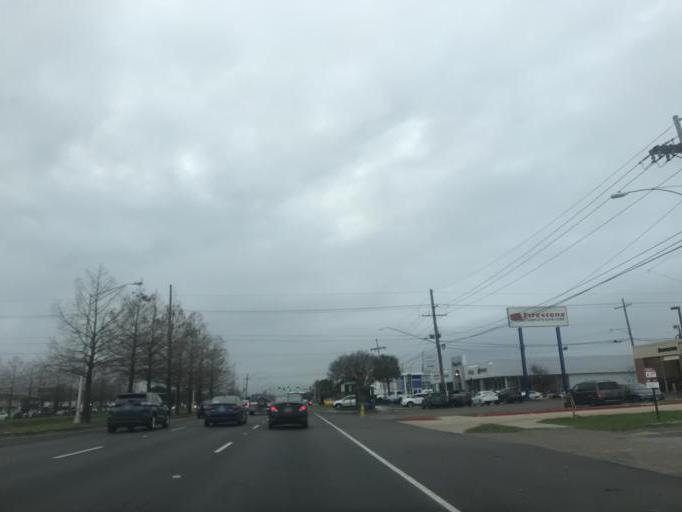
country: US
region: Louisiana
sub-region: Jefferson Parish
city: Metairie
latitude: 30.0038
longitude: -90.1599
